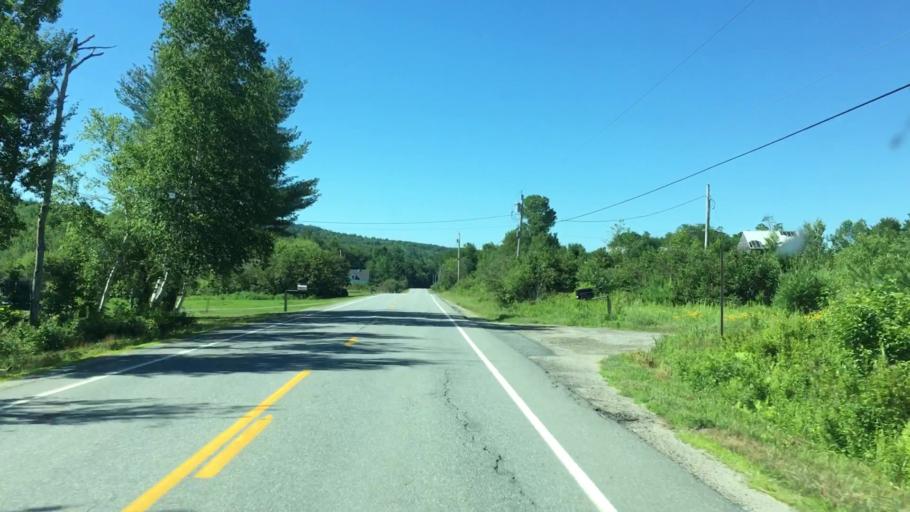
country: US
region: Maine
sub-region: Hancock County
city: Dedham
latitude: 44.6729
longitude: -68.6723
